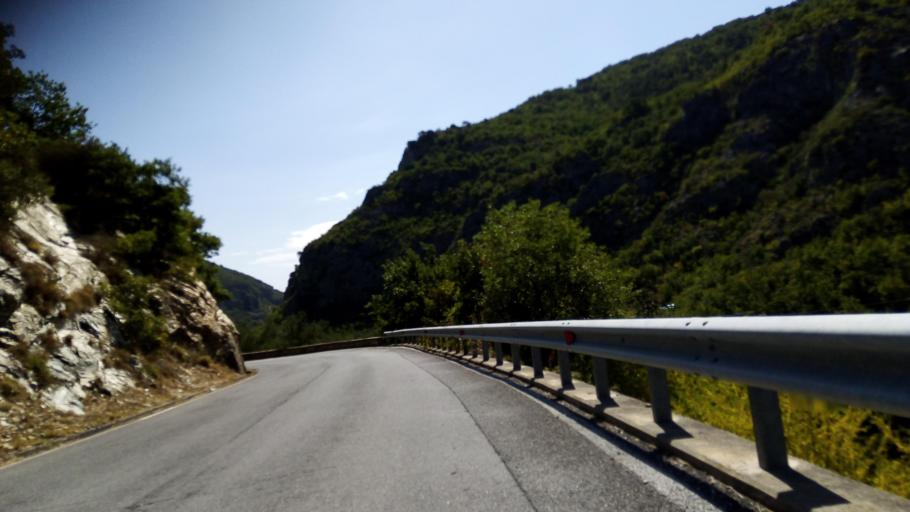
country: IT
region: Liguria
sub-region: Provincia di Savona
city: Balestrino
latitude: 44.1392
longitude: 8.1835
